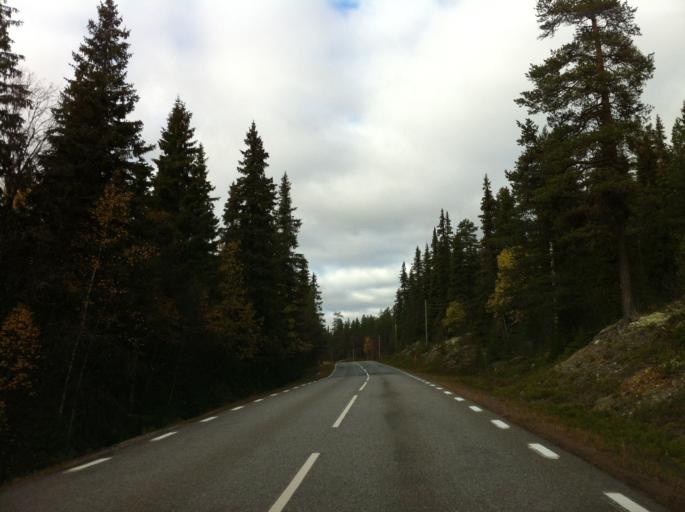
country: NO
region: Hedmark
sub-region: Engerdal
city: Engerdal
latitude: 61.9948
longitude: 12.4597
